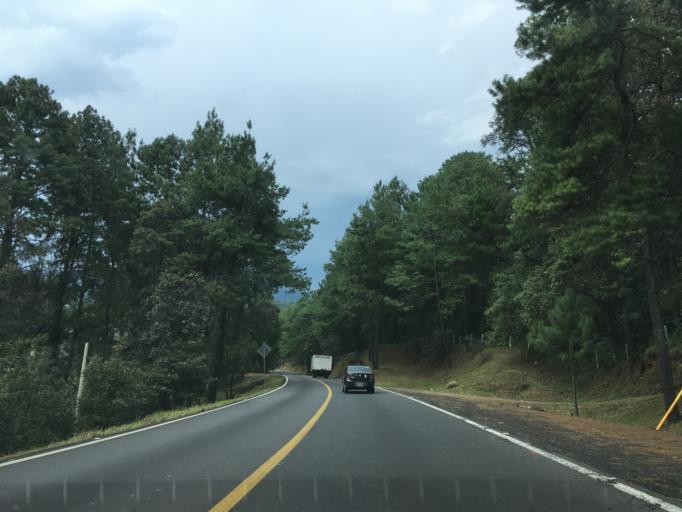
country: MX
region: Michoacan
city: Tingambato
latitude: 19.5028
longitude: -101.8315
